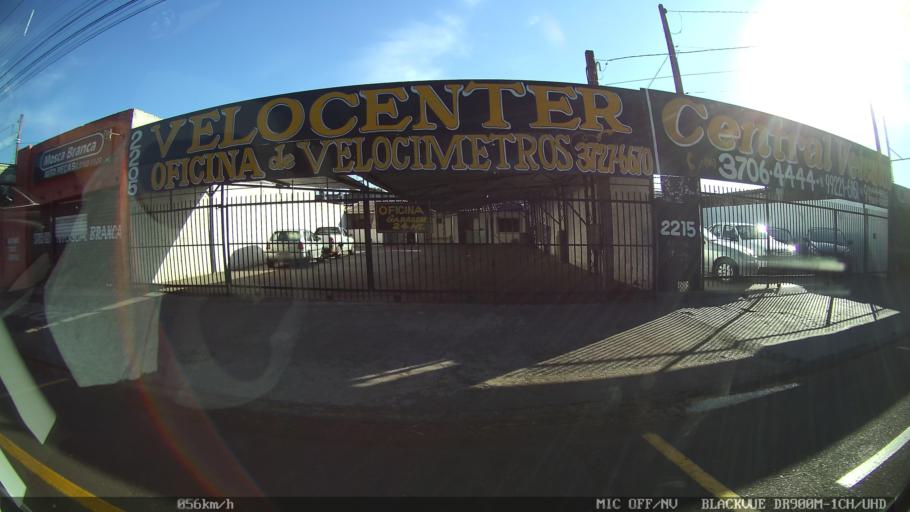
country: BR
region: Sao Paulo
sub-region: Franca
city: Franca
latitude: -20.5135
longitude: -47.3991
